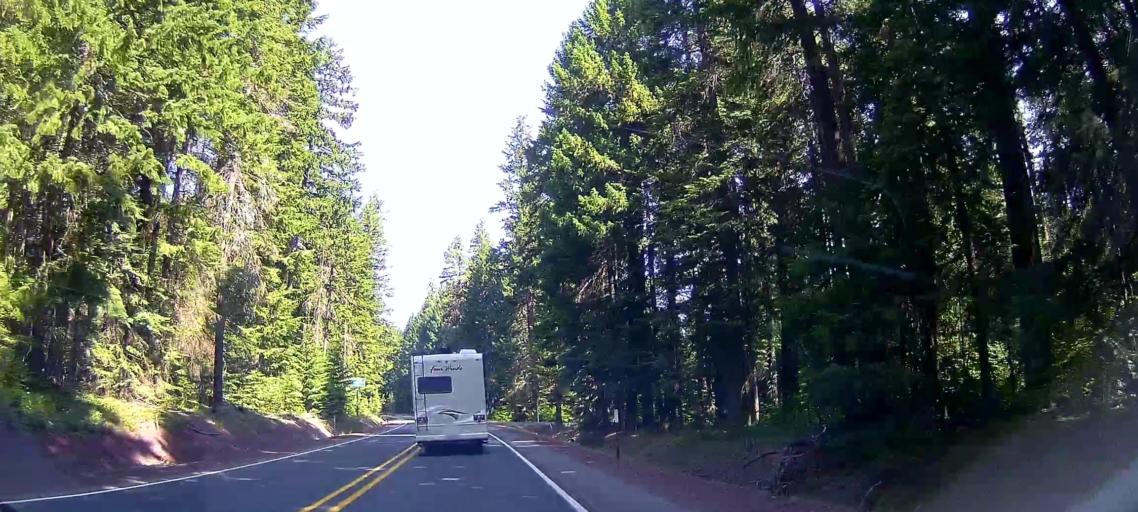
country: US
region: Oregon
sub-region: Jefferson County
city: Warm Springs
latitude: 45.0867
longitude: -121.5448
